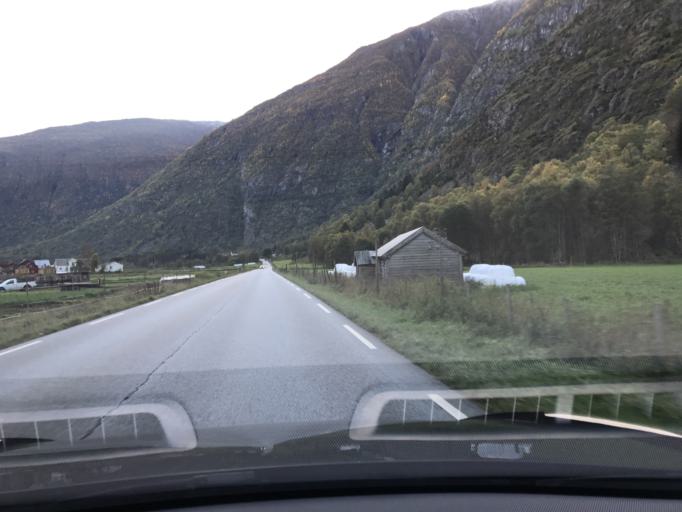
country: NO
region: Sogn og Fjordane
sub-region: Laerdal
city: Laerdalsoyri
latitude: 61.0827
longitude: 7.5079
